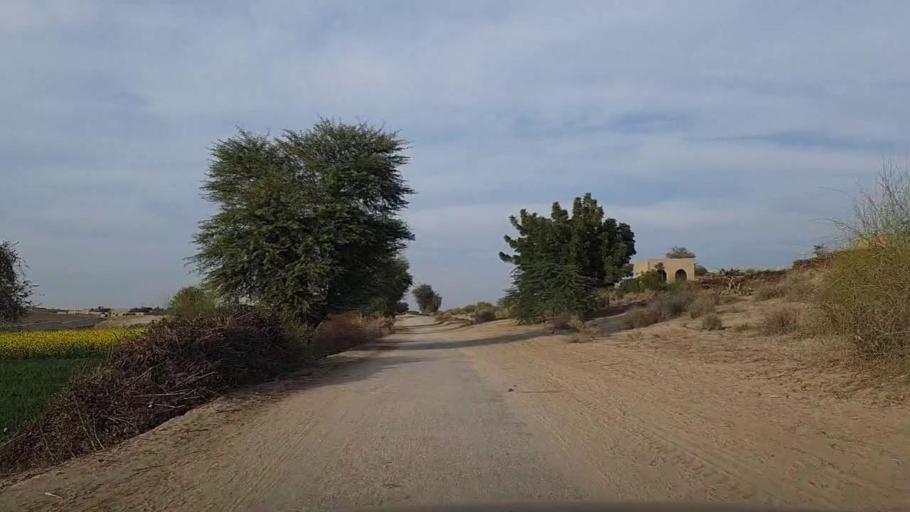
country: PK
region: Sindh
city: Jam Sahib
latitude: 26.4563
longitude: 68.5699
